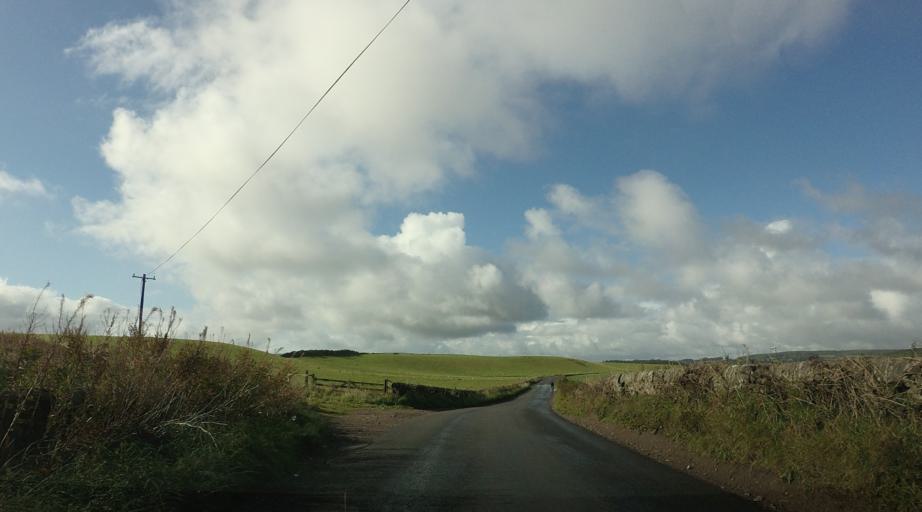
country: GB
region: Scotland
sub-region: Fife
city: Balmullo
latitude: 56.3992
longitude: -2.9137
